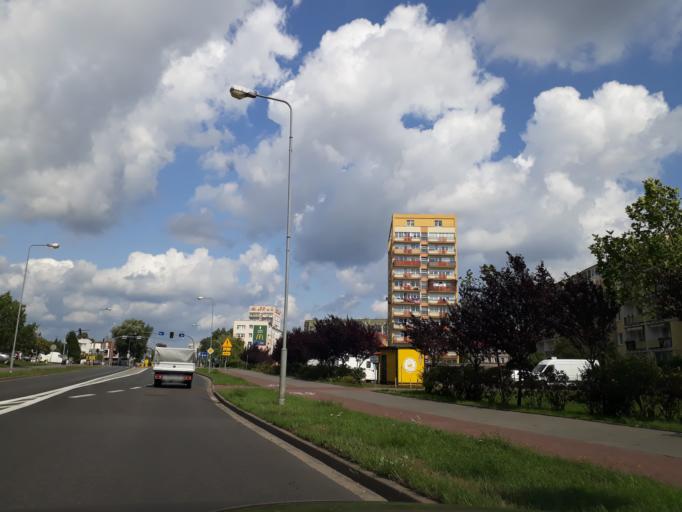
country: PL
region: West Pomeranian Voivodeship
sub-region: Swinoujscie
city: Swinoujscie
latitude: 53.9037
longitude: 14.2361
